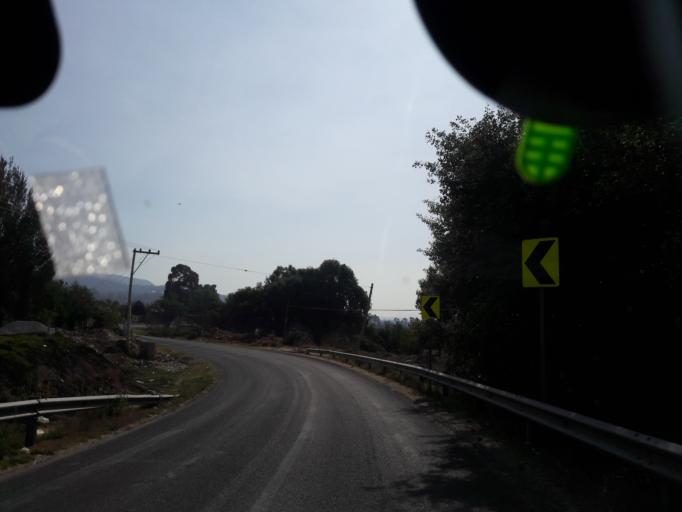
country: MX
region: Tlaxcala
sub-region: Panotla
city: Fraccionamiento la Virgen
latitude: 19.3201
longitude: -98.3047
